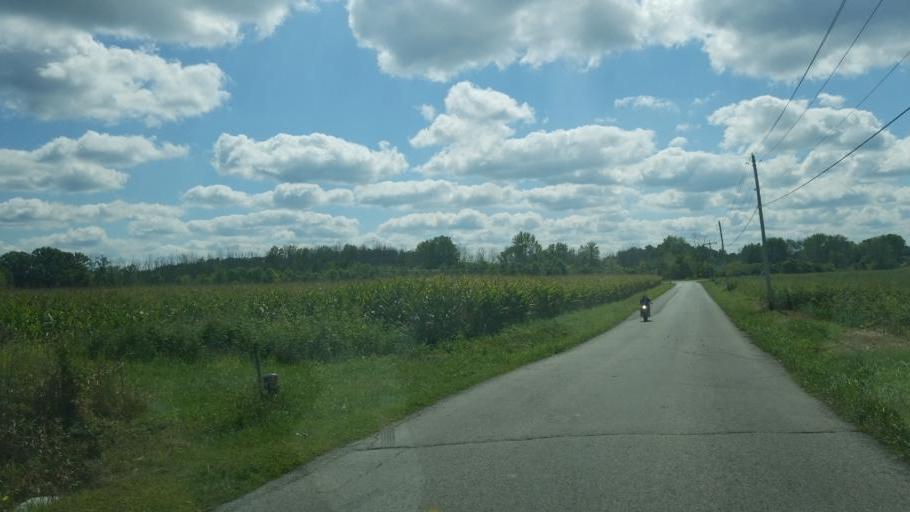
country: US
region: Ohio
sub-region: Ashland County
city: Ashland
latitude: 40.8895
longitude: -82.2785
